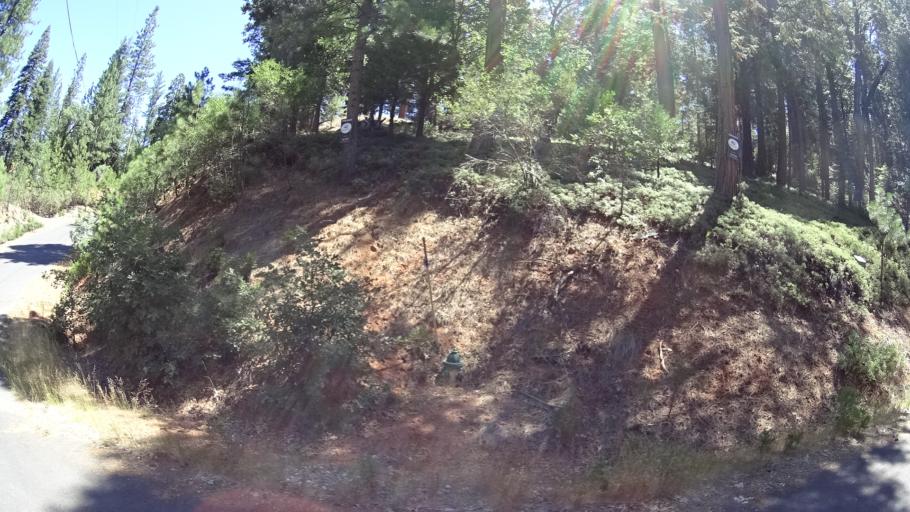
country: US
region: California
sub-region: Calaveras County
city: Arnold
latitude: 38.2310
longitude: -120.3462
